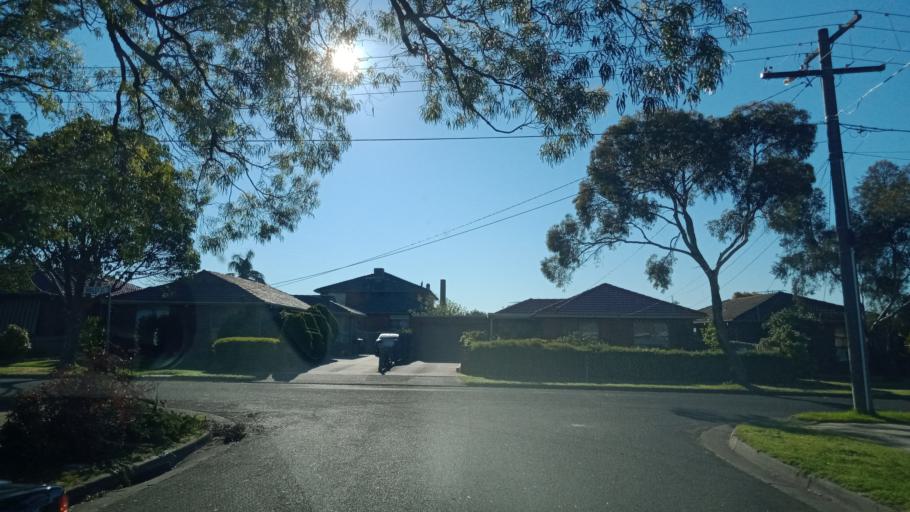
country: AU
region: Victoria
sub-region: Greater Dandenong
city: Noble Park North
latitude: -37.9377
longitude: 145.1858
